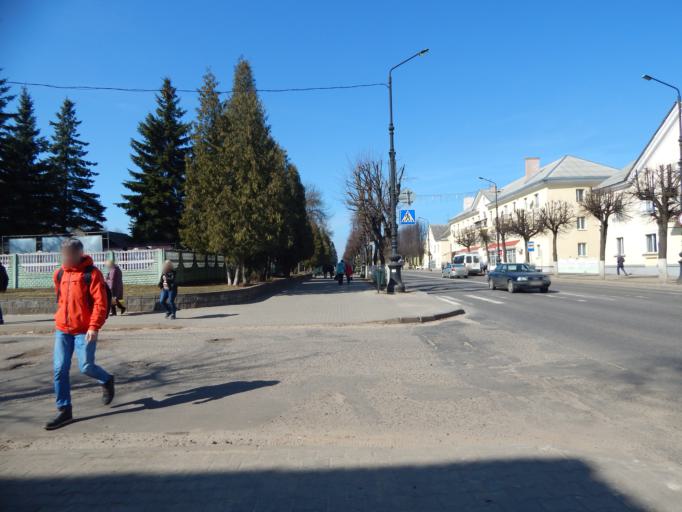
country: BY
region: Minsk
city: Horad Barysaw
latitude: 54.2221
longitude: 28.5208
